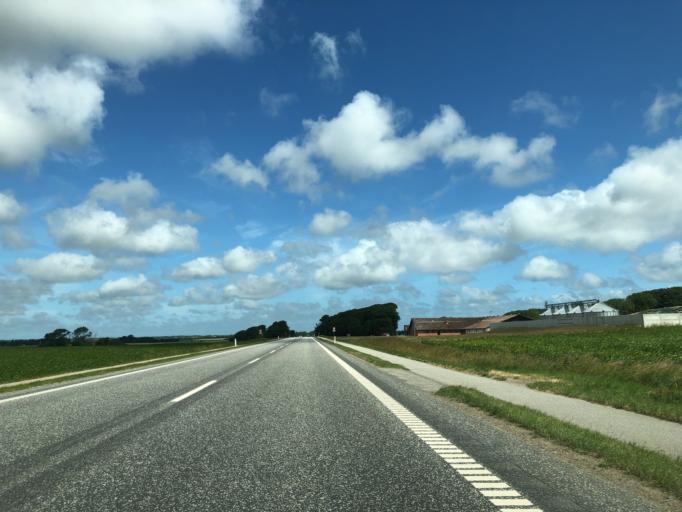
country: DK
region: Central Jutland
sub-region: Holstebro Kommune
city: Holstebro
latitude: 56.4245
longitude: 8.5999
